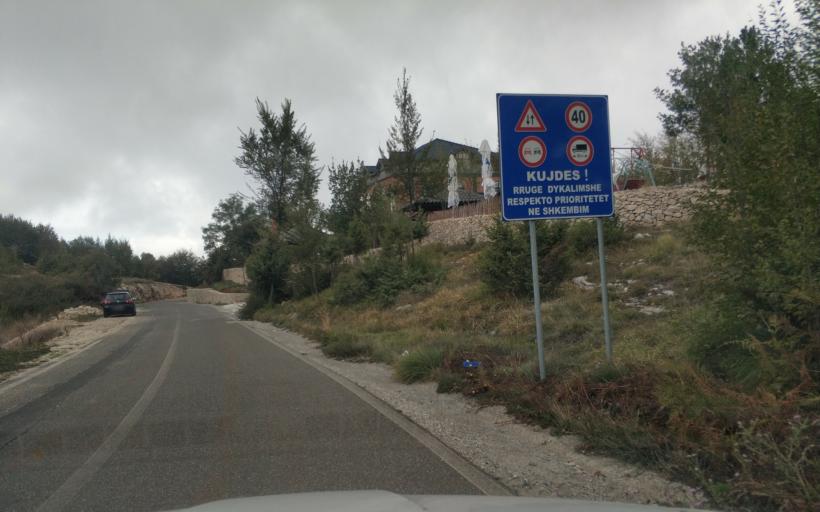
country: AL
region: Durres
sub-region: Rrethi i Krujes
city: Kruje
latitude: 41.5185
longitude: 19.8034
